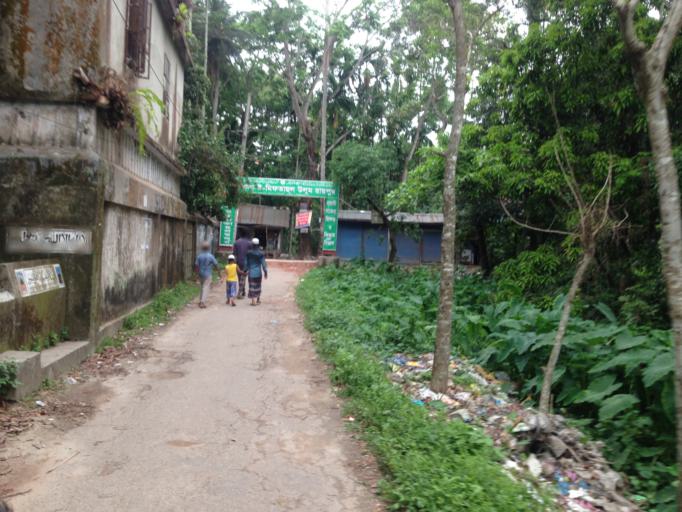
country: BD
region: Chittagong
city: Raipur
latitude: 23.0355
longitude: 90.7715
